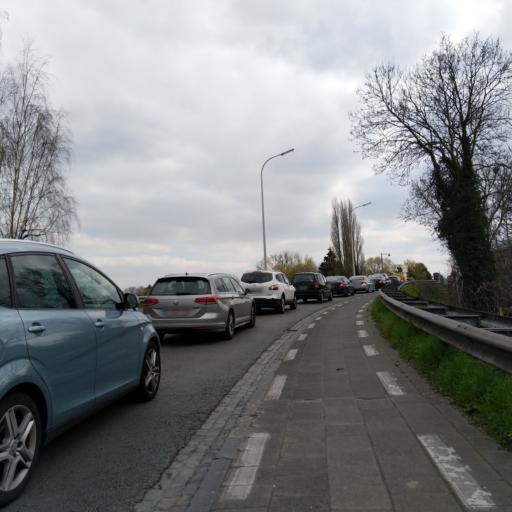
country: BE
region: Wallonia
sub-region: Province du Hainaut
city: Mons
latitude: 50.4729
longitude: 3.9568
